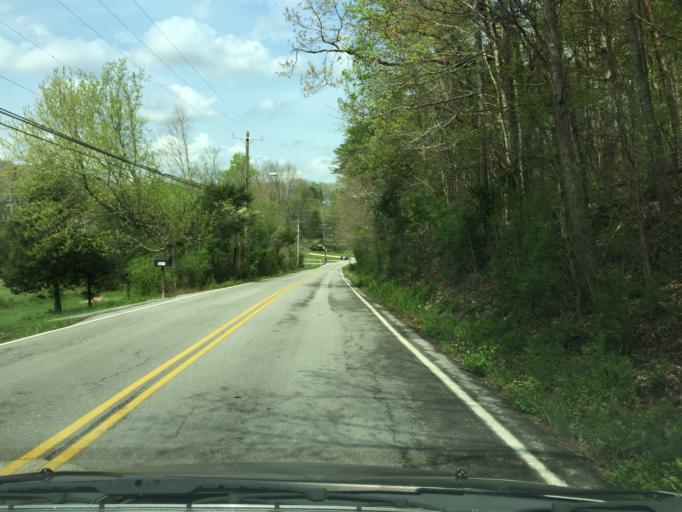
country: US
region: Tennessee
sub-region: Hamilton County
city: Walden
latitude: 35.1449
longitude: -85.2877
